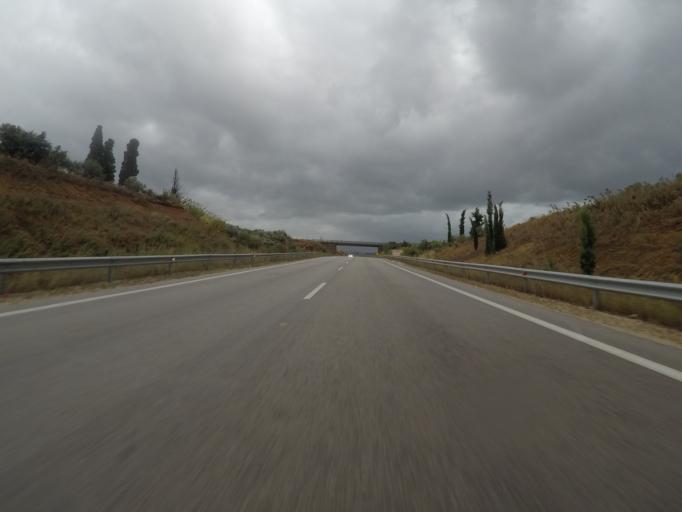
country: GR
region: Peloponnese
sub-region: Nomos Messinias
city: Gargalianoi
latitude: 37.0064
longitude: 21.6604
